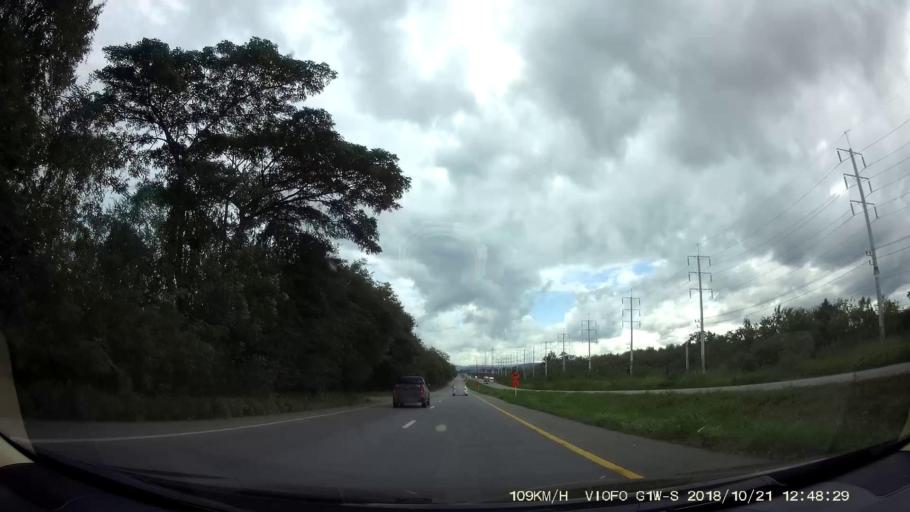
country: TH
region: Nakhon Ratchasima
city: Amphoe Sikhiu
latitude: 14.9118
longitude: 101.6840
